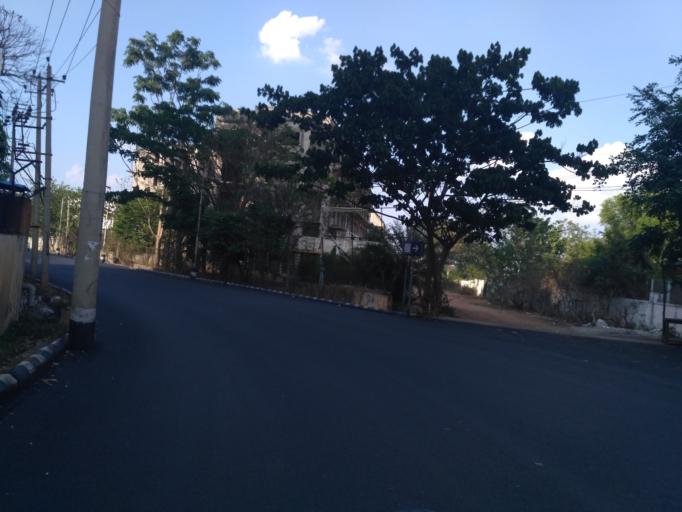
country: IN
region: Karnataka
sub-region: Bangalore Urban
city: Yelahanka
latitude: 13.0382
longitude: 77.5376
